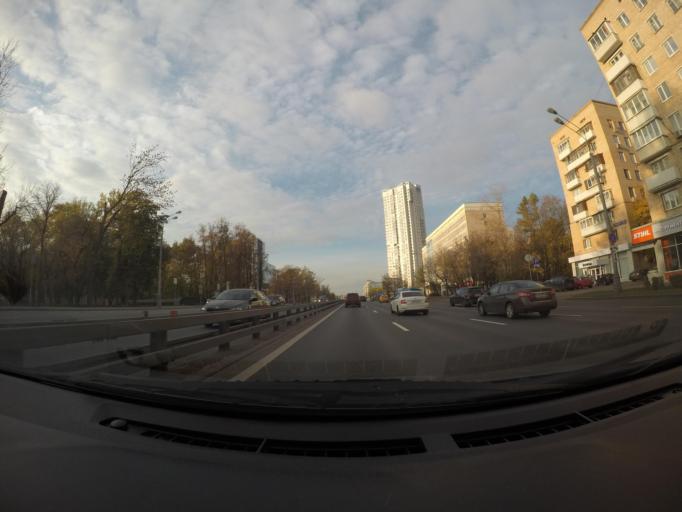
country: RU
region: Moskovskaya
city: Levoberezhnyy
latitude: 55.8578
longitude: 37.4684
